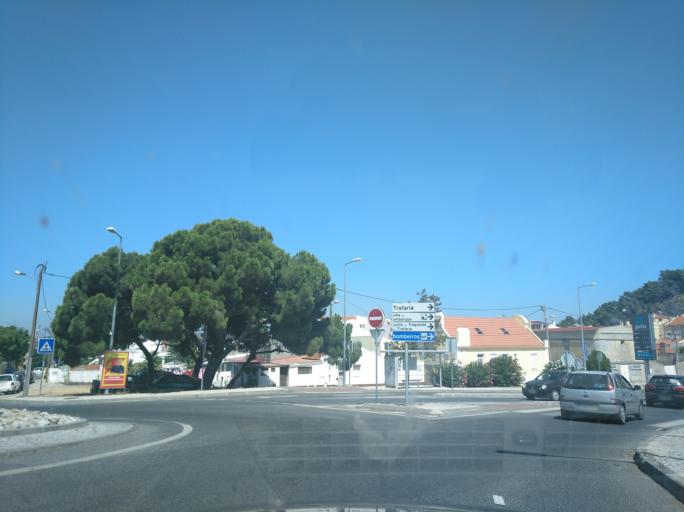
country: PT
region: Setubal
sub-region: Almada
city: Trafaria
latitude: 38.6696
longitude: -9.2332
